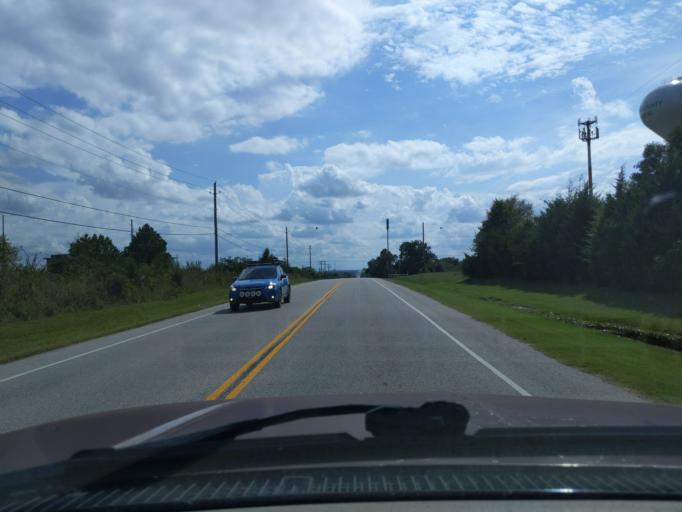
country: US
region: Oklahoma
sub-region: Tulsa County
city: Jenks
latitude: 36.0489
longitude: -96.0116
